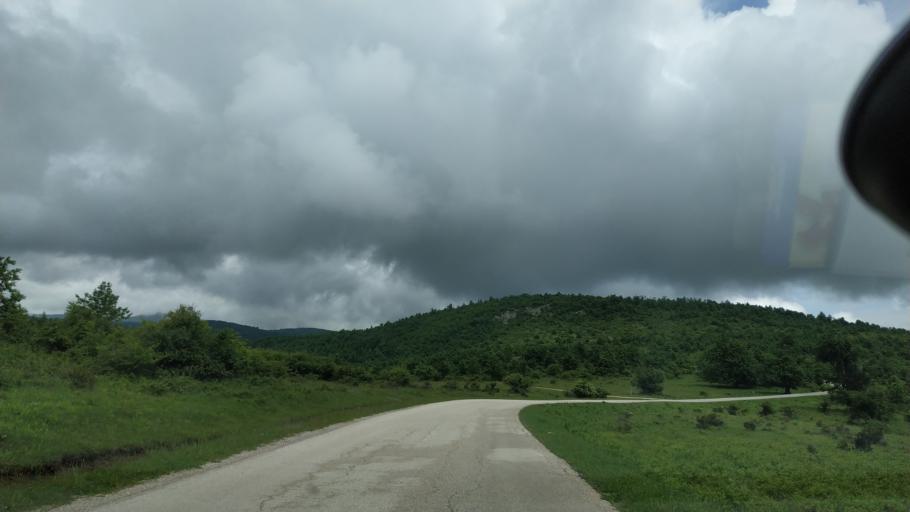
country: RS
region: Central Serbia
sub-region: Zajecarski Okrug
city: Soko Banja
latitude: 43.7128
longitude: 21.9395
